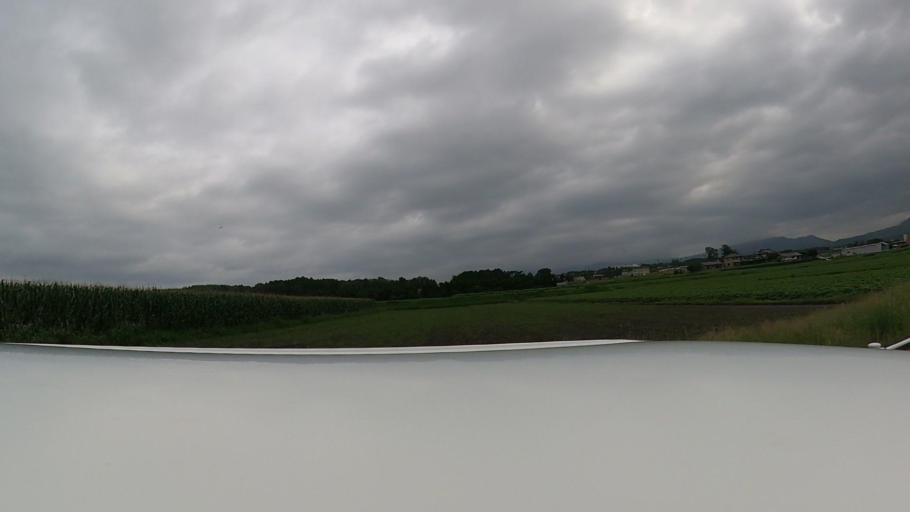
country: JP
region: Kumamoto
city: Ozu
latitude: 32.8380
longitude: 130.9003
